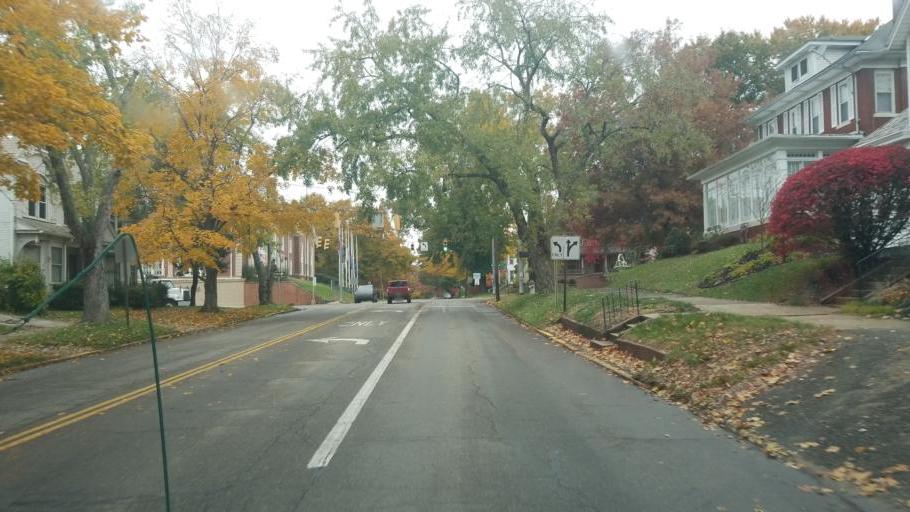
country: US
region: Ohio
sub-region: Washington County
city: Marietta
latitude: 39.4209
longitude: -81.4602
